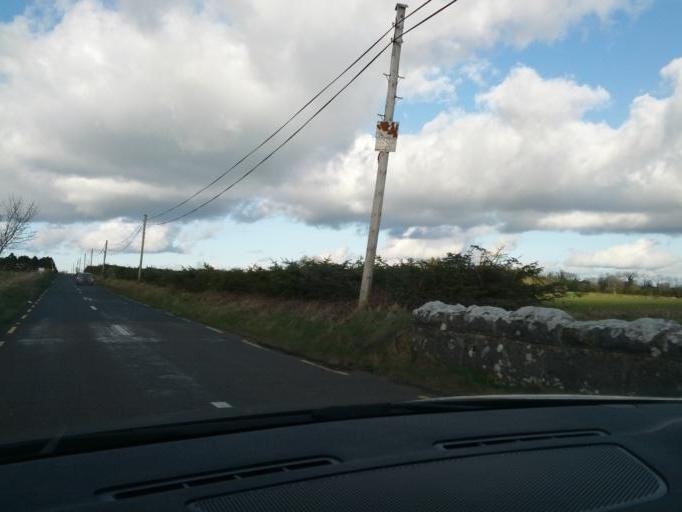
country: IE
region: Connaught
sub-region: Roscommon
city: Castlerea
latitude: 53.6466
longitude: -8.5234
